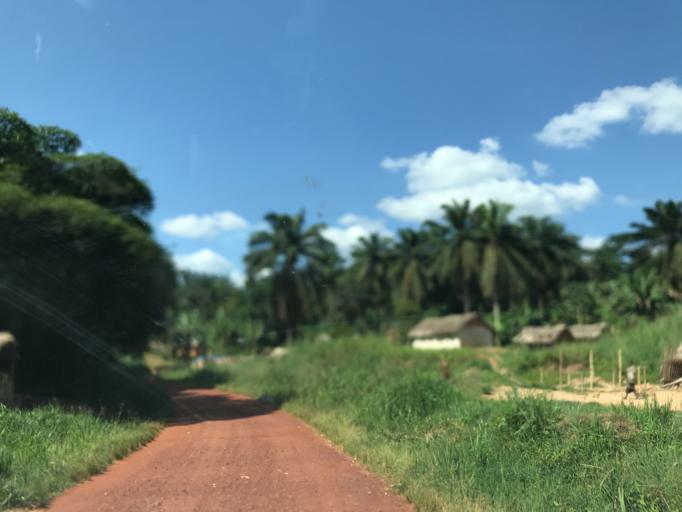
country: CD
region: Eastern Province
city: Kisangani
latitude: 1.2523
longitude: 25.2761
